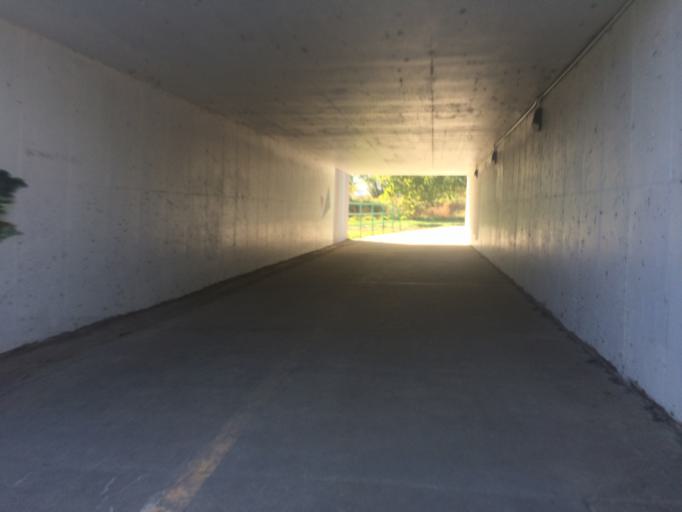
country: US
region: Colorado
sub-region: Broomfield County
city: Broomfield
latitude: 39.8785
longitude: -105.0760
